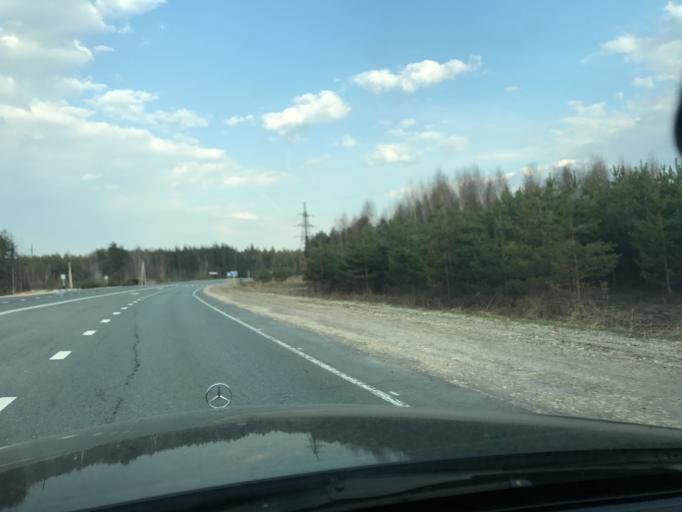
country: RU
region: Vladimir
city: Andreyevo
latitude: 55.9355
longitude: 41.0938
